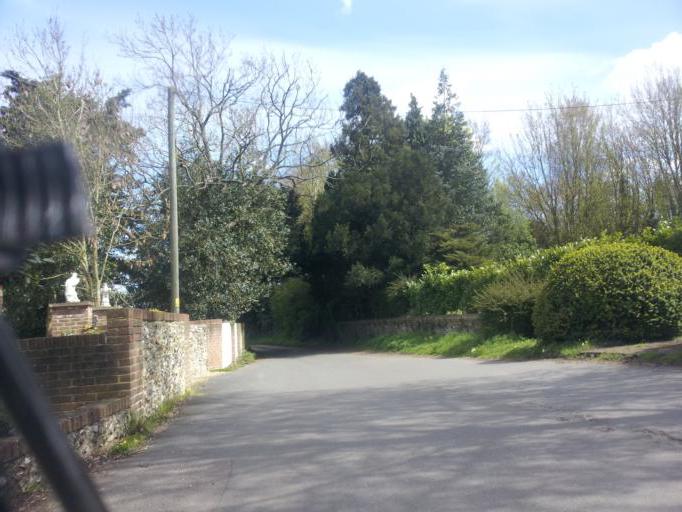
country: GB
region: England
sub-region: Kent
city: Rainham
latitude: 51.3300
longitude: 0.6146
